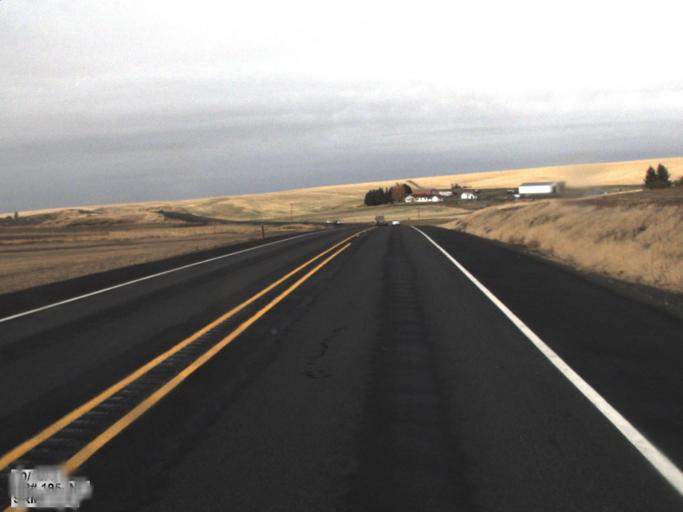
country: US
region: Washington
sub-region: Whitman County
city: Pullman
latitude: 46.5804
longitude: -117.1536
